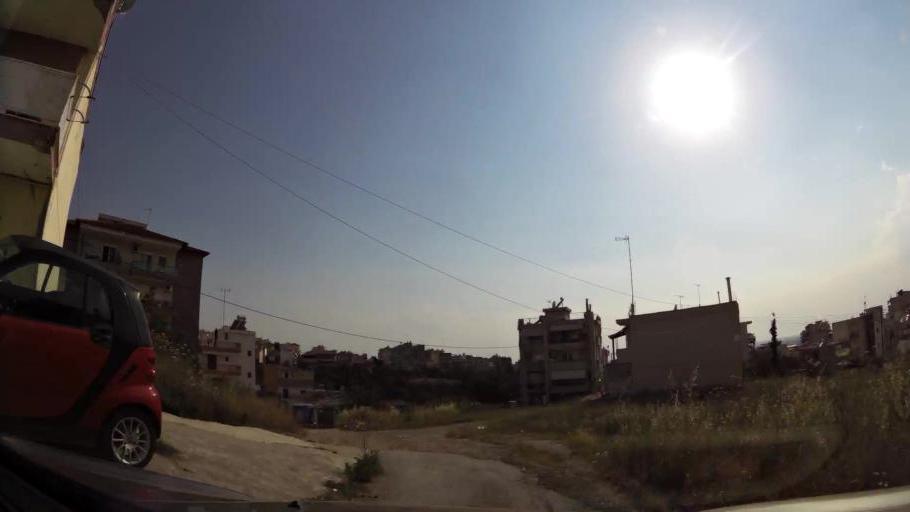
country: GR
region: Central Macedonia
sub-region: Nomos Thessalonikis
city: Polichni
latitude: 40.6595
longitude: 22.9525
